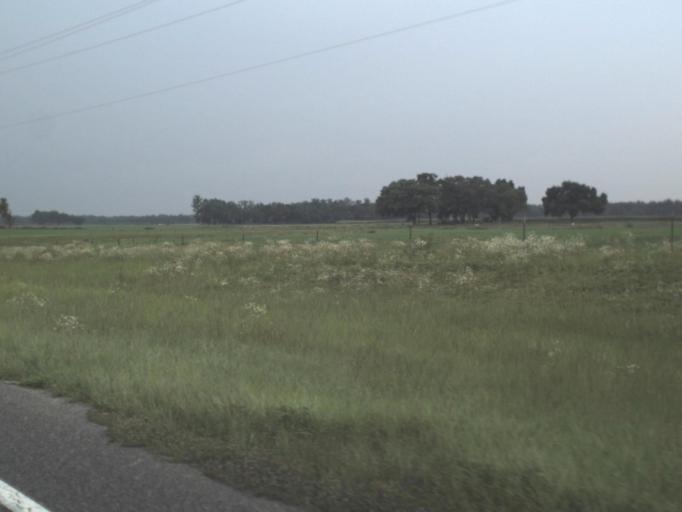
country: US
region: Florida
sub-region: Levy County
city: Chiefland
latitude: 29.4748
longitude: -82.7890
